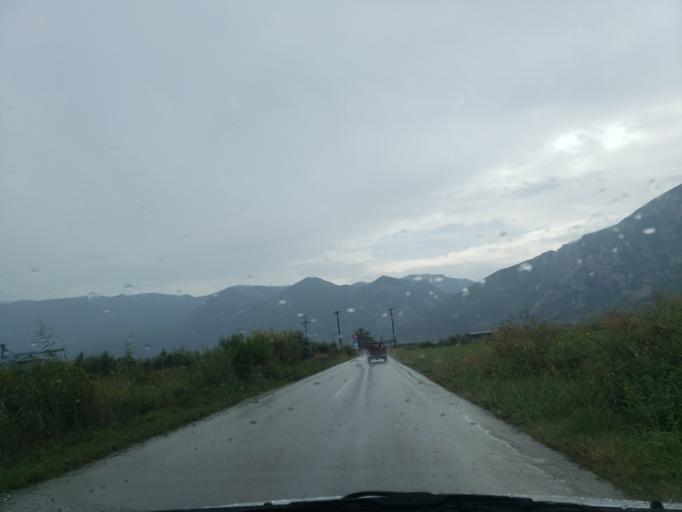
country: GR
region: Central Greece
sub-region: Nomos Fthiotidos
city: Anthili
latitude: 38.8138
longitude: 22.4422
